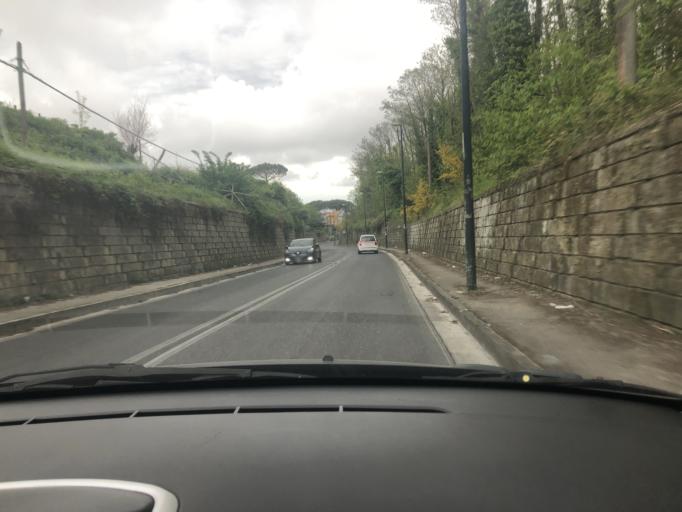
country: IT
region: Campania
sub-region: Provincia di Napoli
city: Torre Caracciolo
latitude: 40.8640
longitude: 14.1933
